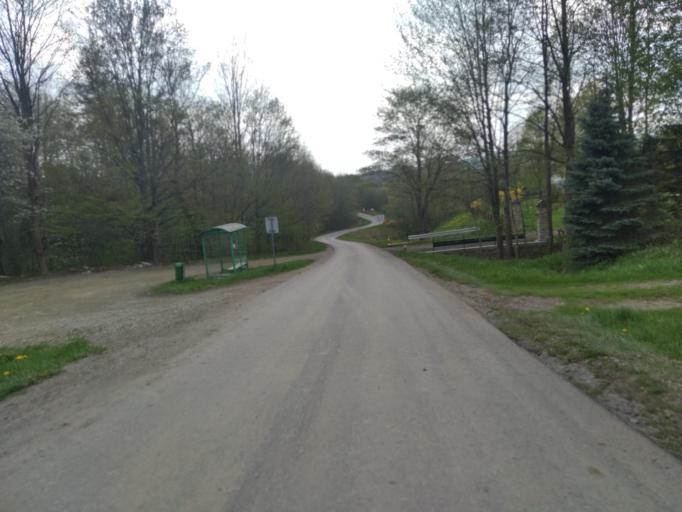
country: PL
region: Subcarpathian Voivodeship
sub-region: Powiat krosnienski
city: Iwonicz-Zdroj
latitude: 49.5317
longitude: 21.8024
